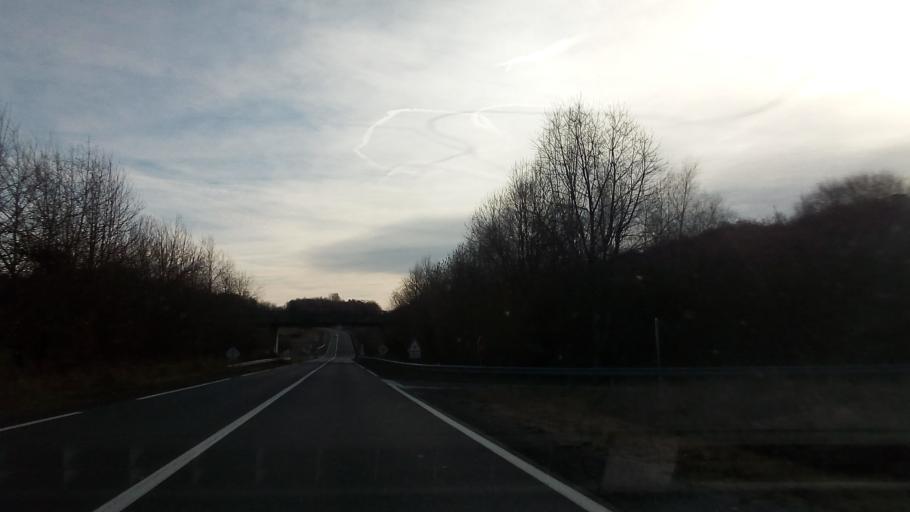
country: FR
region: Limousin
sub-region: Departement de la Correze
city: Seilhac
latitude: 45.3600
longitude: 1.7119
